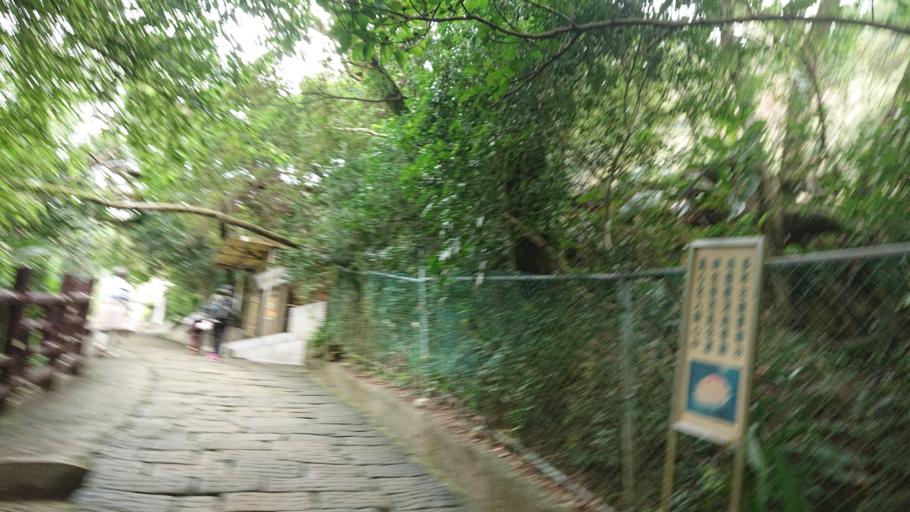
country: TW
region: Taipei
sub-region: Taipei
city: Banqiao
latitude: 24.9525
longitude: 121.4446
